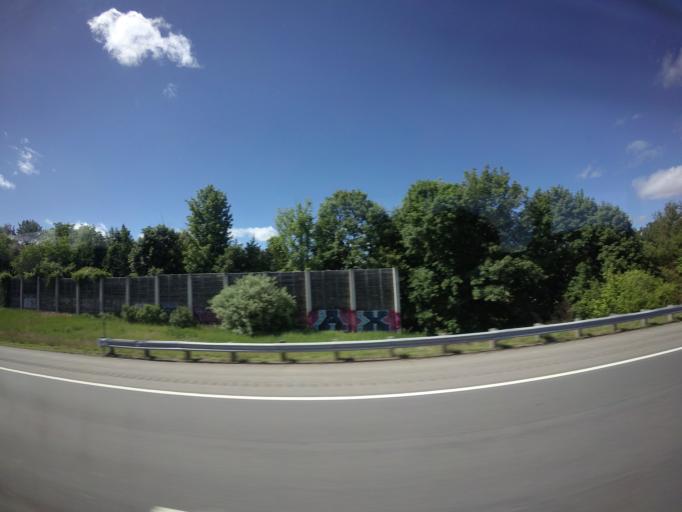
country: US
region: New Hampshire
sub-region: Hillsborough County
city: Manchester
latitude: 42.9606
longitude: -71.4229
